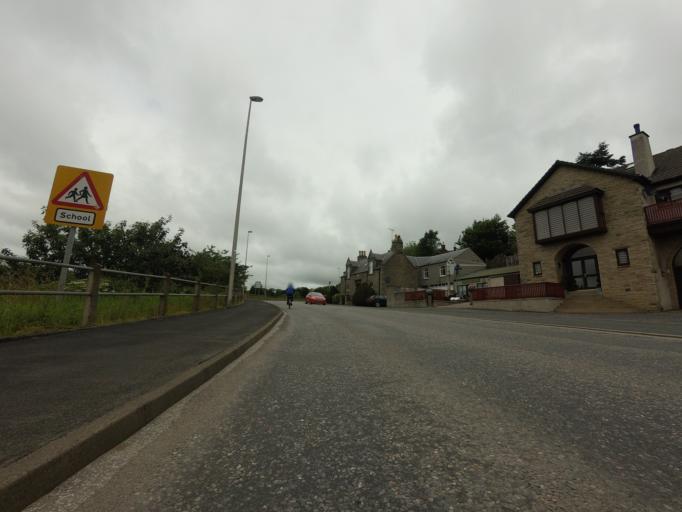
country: GB
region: Scotland
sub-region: Aberdeenshire
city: Turriff
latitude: 57.5355
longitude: -2.4623
